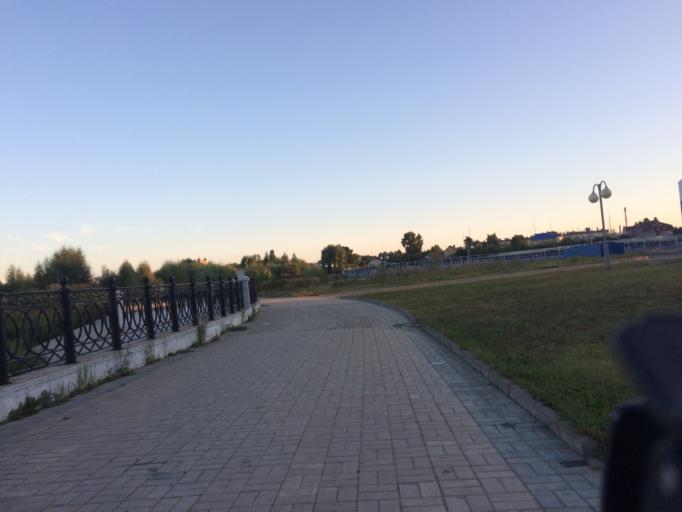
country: RU
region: Mariy-El
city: Yoshkar-Ola
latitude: 56.6241
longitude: 47.8961
